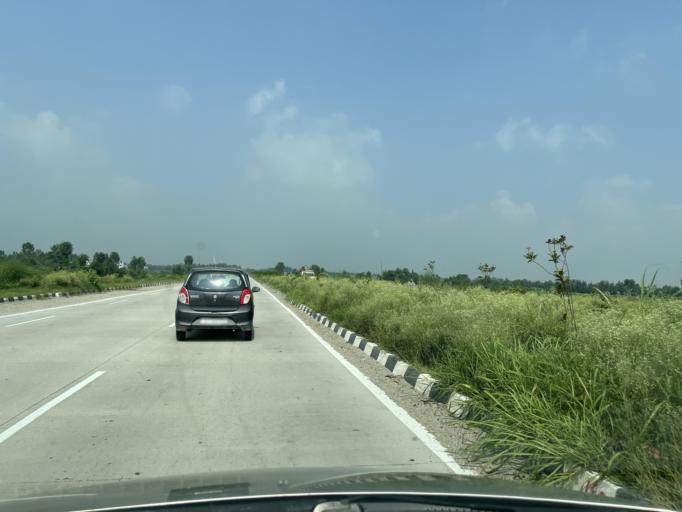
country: IN
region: Uttarakhand
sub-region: Udham Singh Nagar
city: Kashipur
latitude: 29.1633
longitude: 78.9952
